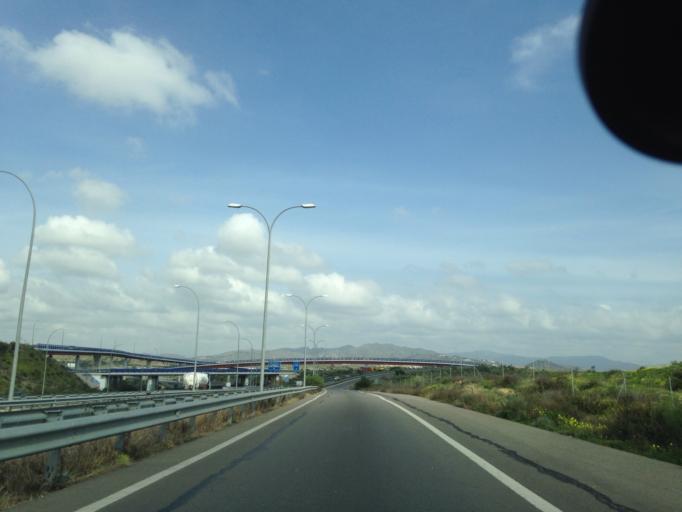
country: ES
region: Andalusia
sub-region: Provincia de Malaga
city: Alhaurin de la Torre
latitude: 36.7095
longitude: -4.5111
